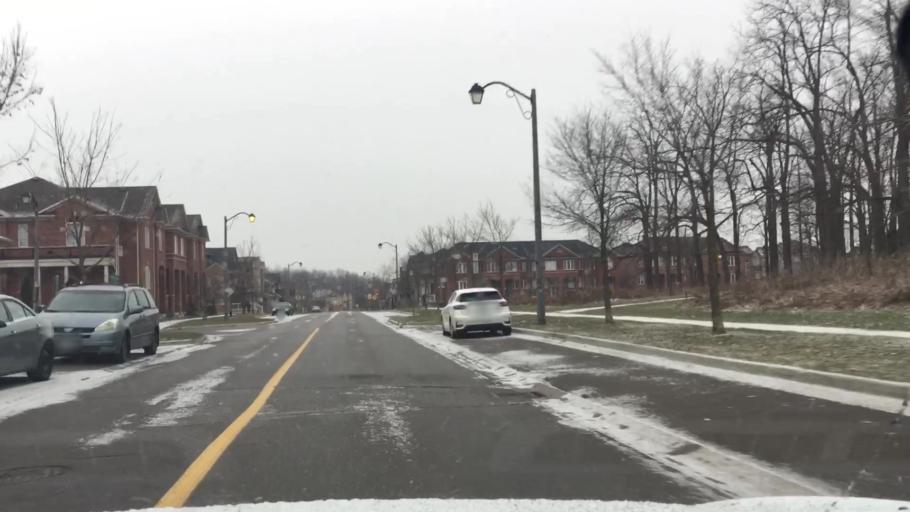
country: CA
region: Ontario
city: Markham
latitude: 43.8974
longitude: -79.2200
